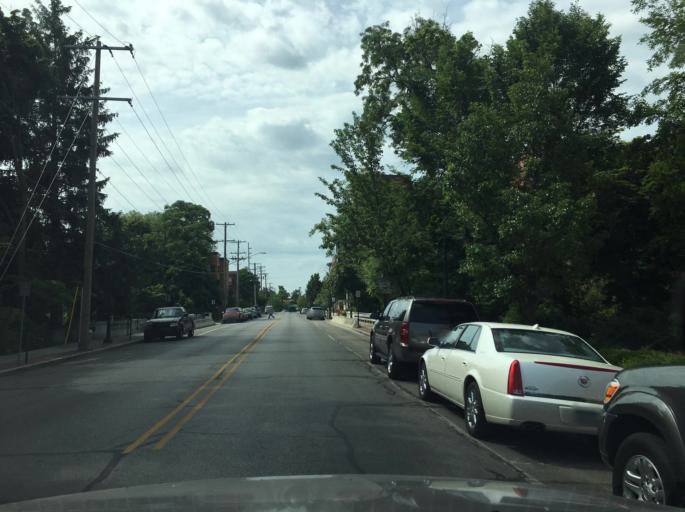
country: US
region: Michigan
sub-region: Grand Traverse County
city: Traverse City
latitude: 44.7619
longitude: -85.6210
